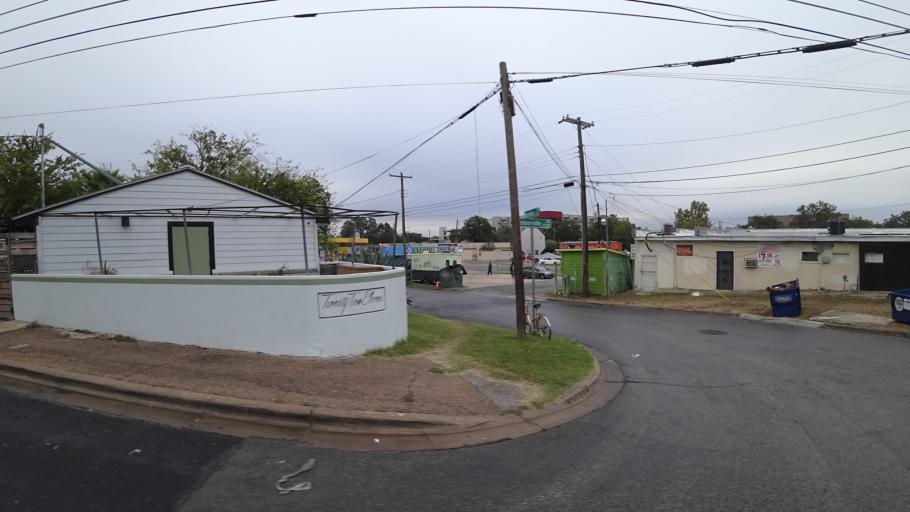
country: US
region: Texas
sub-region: Travis County
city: Austin
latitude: 30.2618
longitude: -97.7166
